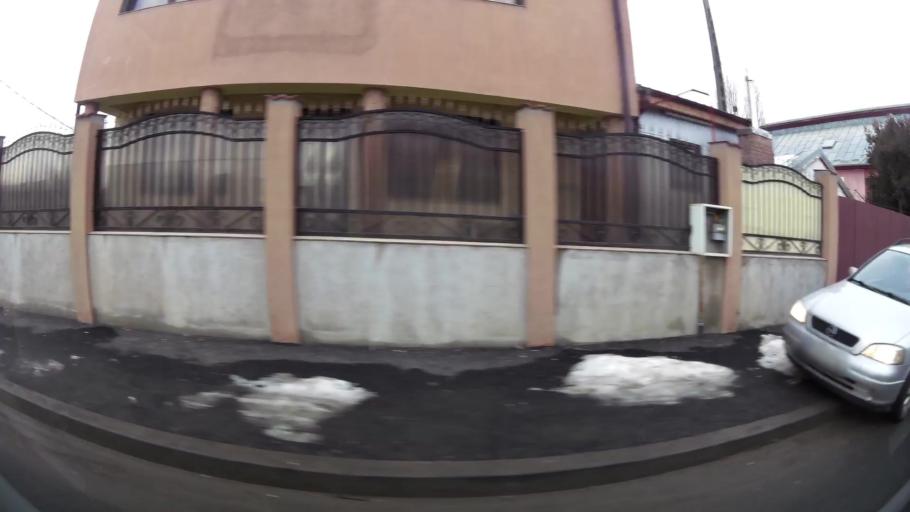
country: RO
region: Ilfov
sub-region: Comuna Pantelimon
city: Pantelimon
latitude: 44.4588
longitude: 26.2098
